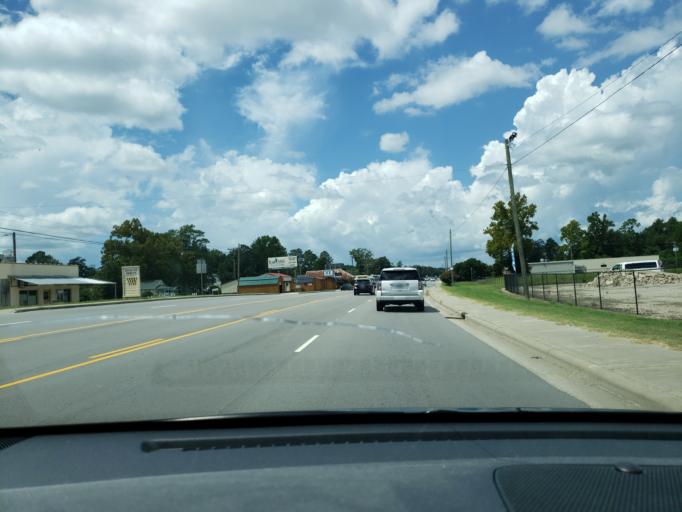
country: US
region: North Carolina
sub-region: Bladen County
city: Bladenboro
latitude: 34.7316
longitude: -78.7876
